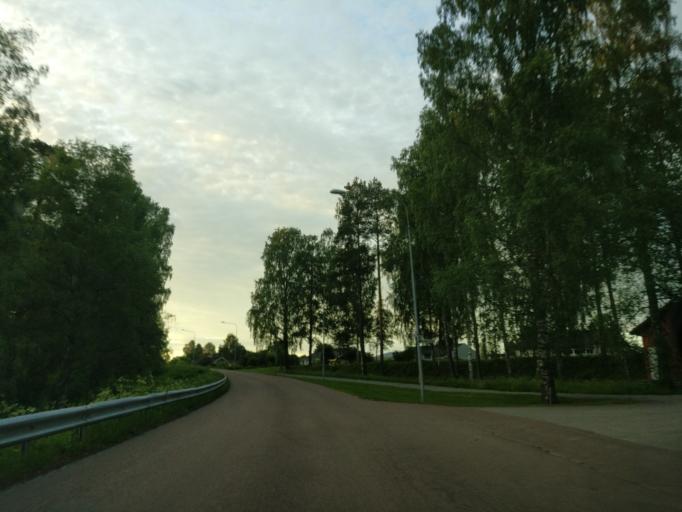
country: SE
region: Vaermland
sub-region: Hagfors Kommun
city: Hagfors
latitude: 60.0021
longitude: 13.5981
